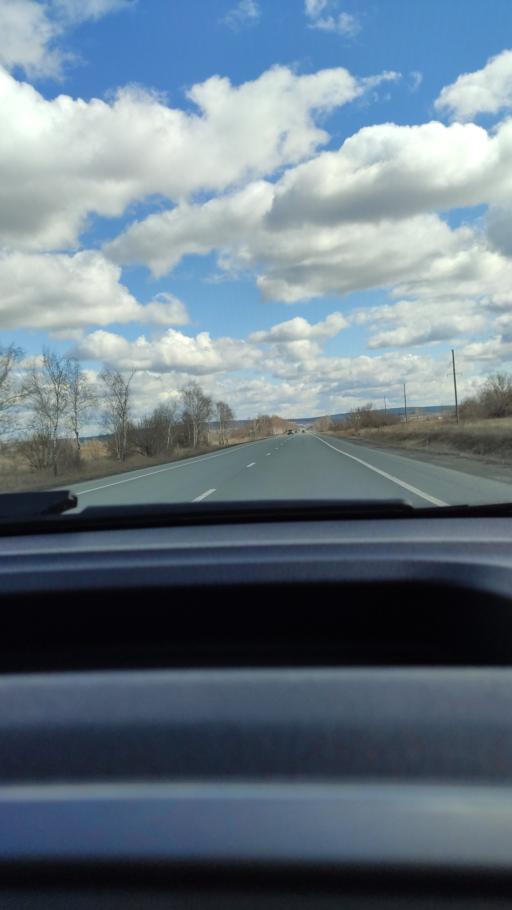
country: RU
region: Samara
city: Kurumoch
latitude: 53.4904
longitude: 49.9813
